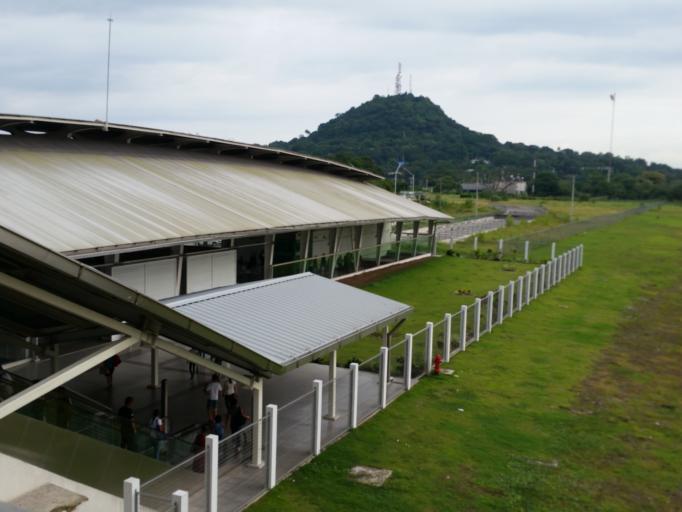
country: PA
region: Panama
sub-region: Distrito de Panama
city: Ancon
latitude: 8.9737
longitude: -79.5496
